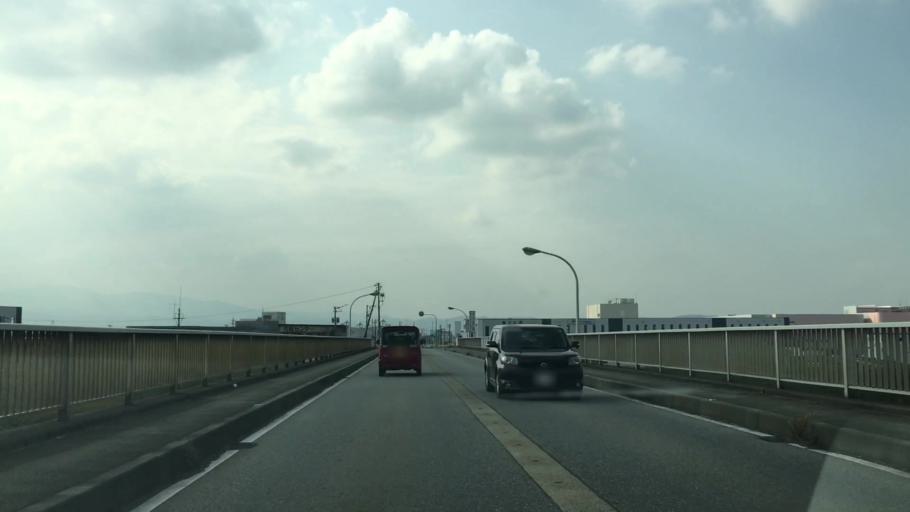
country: JP
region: Toyama
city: Toyama-shi
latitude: 36.6316
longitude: 137.1847
